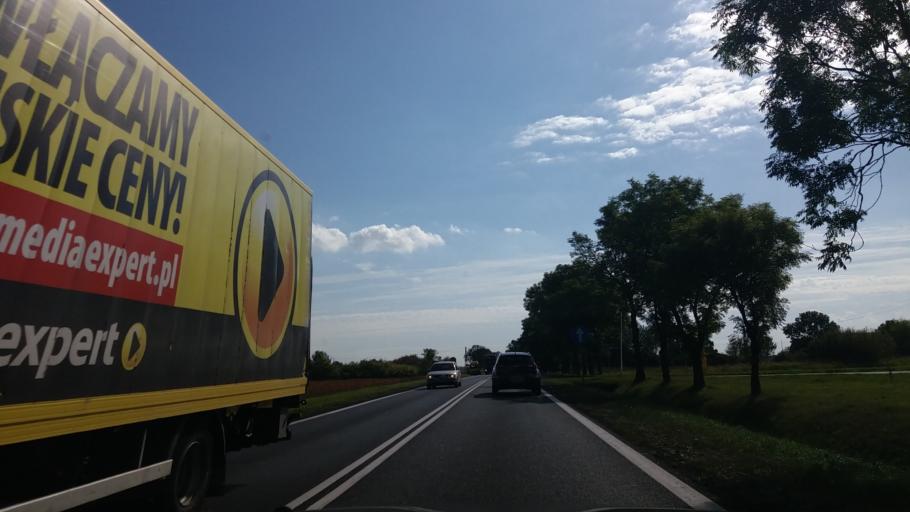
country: PL
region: Lower Silesian Voivodeship
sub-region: Powiat lubinski
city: Osiek
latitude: 51.3334
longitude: 16.3012
